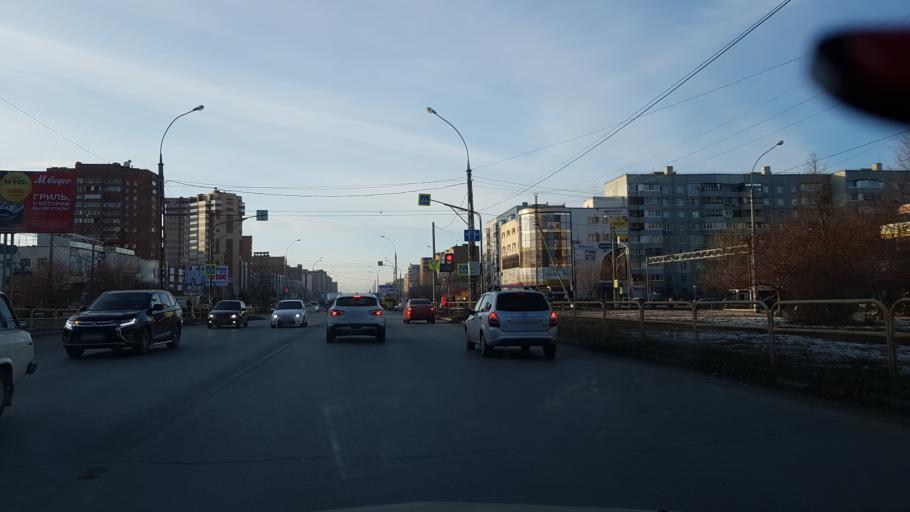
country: RU
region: Samara
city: Tol'yatti
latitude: 53.5410
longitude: 49.3469
